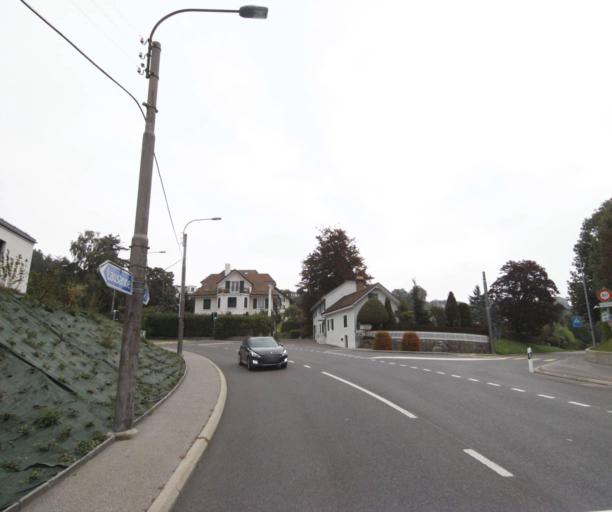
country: CH
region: Vaud
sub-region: Lausanne District
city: Epalinges
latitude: 46.5445
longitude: 6.6678
